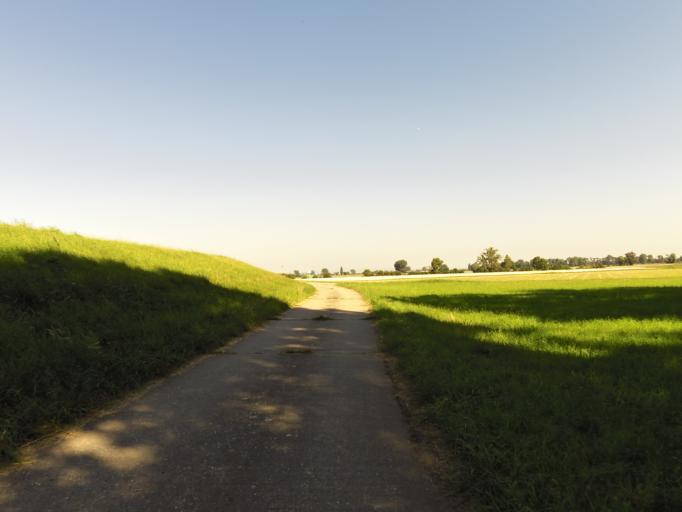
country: DE
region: Rheinland-Pfalz
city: Oppenheim
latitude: 49.8337
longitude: 8.4153
